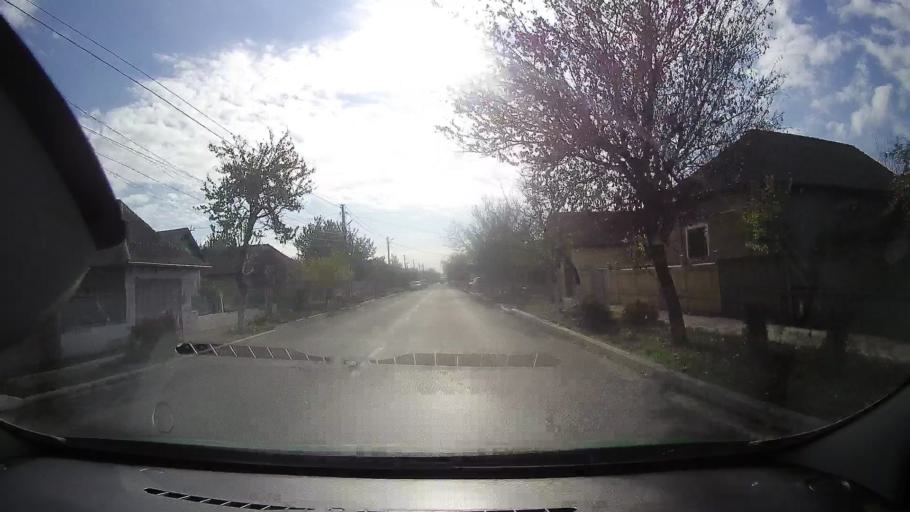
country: RO
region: Tulcea
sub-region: Comuna Sarichioi
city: Sarichioi
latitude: 44.9491
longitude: 28.8518
